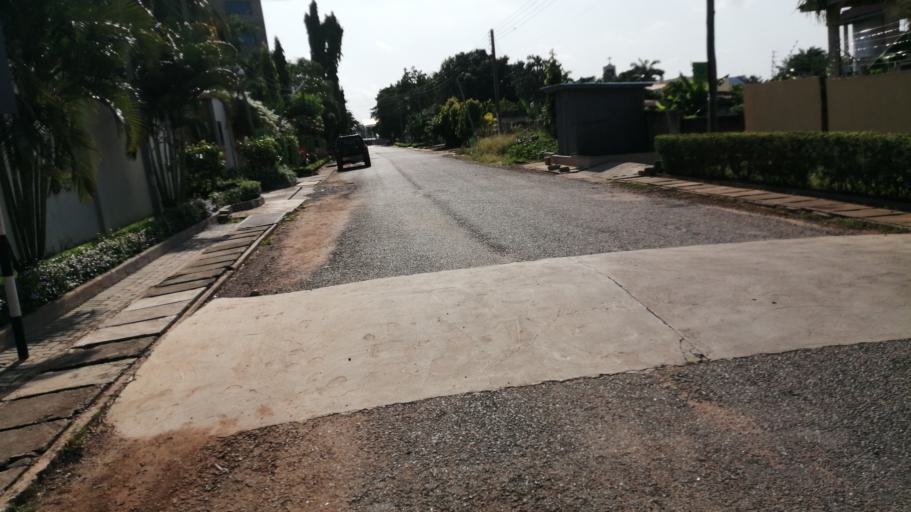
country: GH
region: Greater Accra
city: Medina Estates
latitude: 5.6178
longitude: -0.1825
